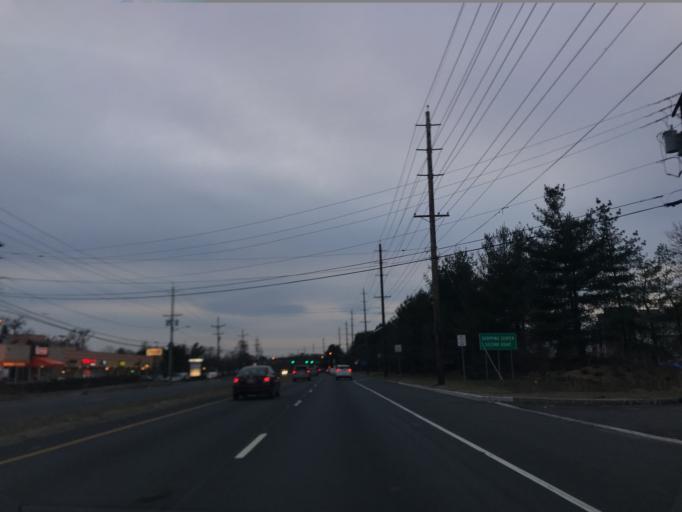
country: US
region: New Jersey
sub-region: Middlesex County
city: Milltown
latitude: 40.4364
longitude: -74.4843
